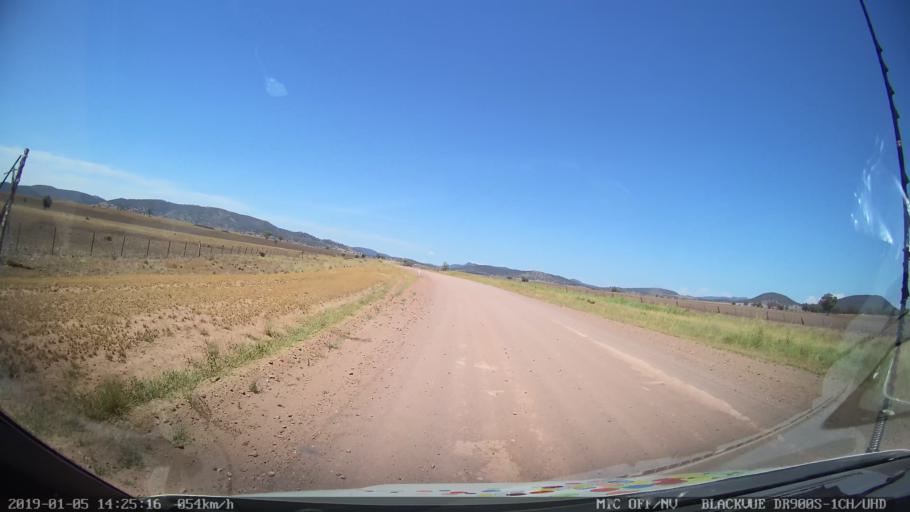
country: AU
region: New South Wales
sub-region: Liverpool Plains
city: Quirindi
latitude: -31.2414
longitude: 150.5482
